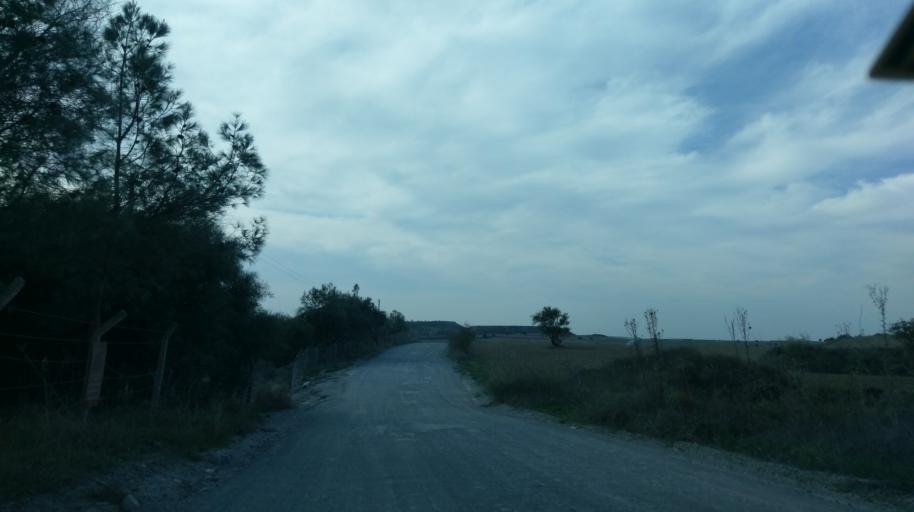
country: CY
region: Keryneia
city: Lapithos
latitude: 35.2834
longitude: 33.1650
